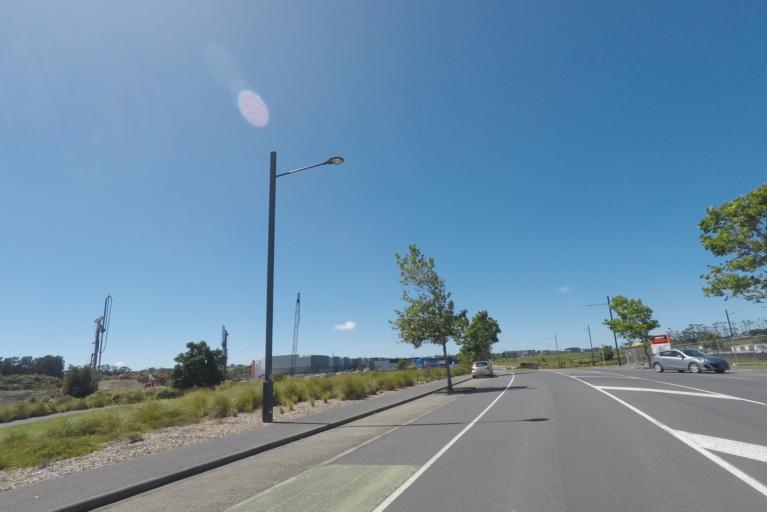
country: NZ
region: Auckland
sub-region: Auckland
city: Rosebank
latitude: -36.8105
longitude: 174.6066
